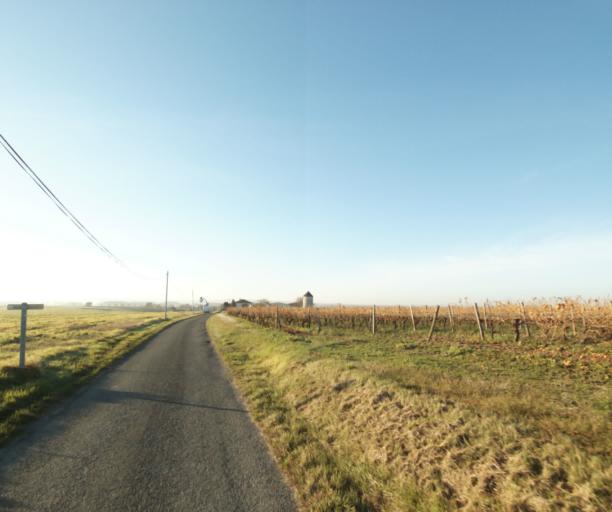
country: FR
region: Poitou-Charentes
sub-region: Departement de la Charente-Maritime
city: Cherac
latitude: 45.6918
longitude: -0.4233
